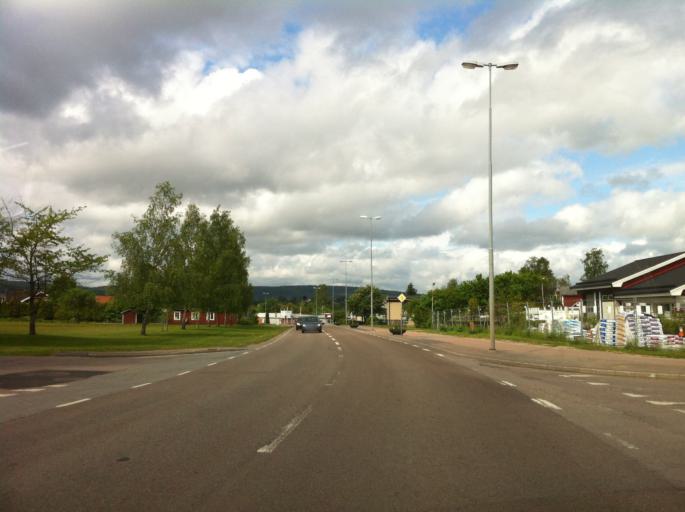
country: SE
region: Vaermland
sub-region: Sunne Kommun
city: Sunne
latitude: 59.8401
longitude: 13.1565
